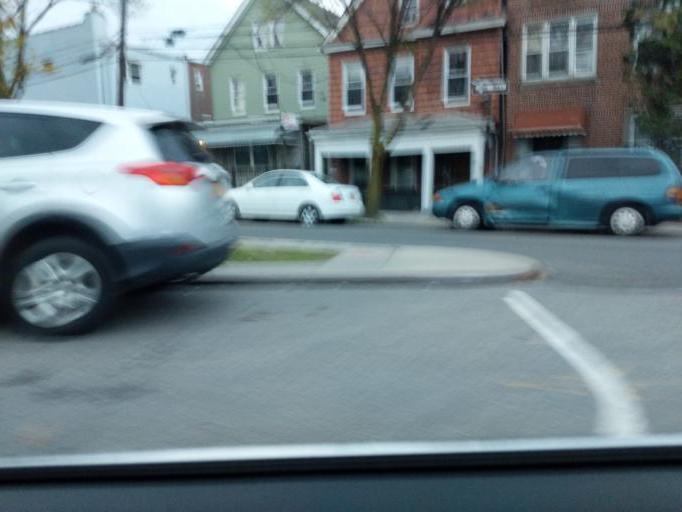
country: US
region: New York
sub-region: Bronx
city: The Bronx
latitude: 40.8483
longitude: -73.8672
